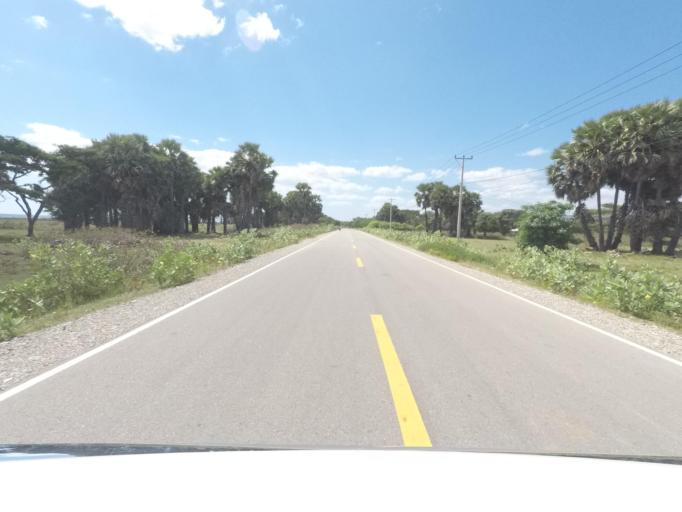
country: TL
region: Lautem
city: Lospalos
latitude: -8.3953
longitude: 126.8398
